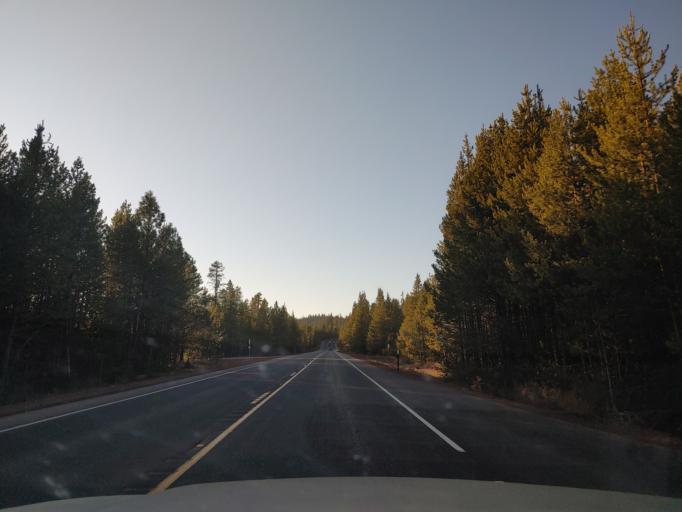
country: US
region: Oregon
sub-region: Deschutes County
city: La Pine
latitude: 43.4397
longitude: -121.8644
